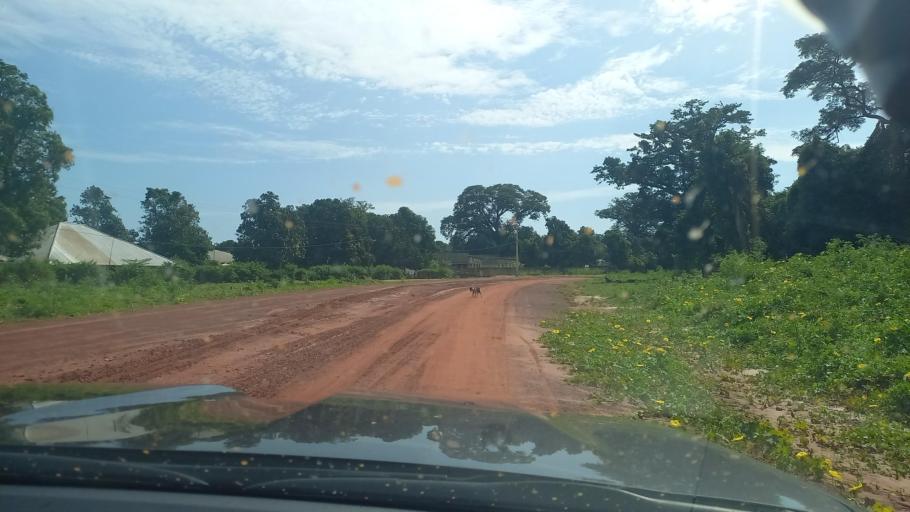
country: SN
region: Ziguinchor
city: Ziguinchor
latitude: 12.6757
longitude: -16.1979
